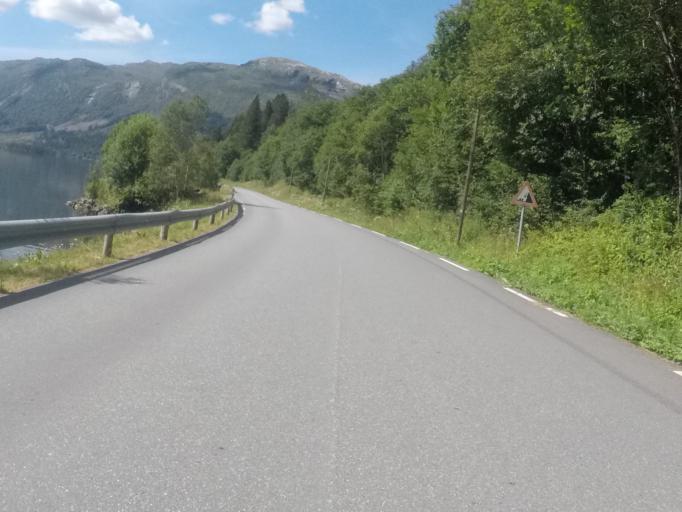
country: NO
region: Sogn og Fjordane
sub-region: Hoyanger
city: Hoyanger
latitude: 61.3586
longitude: 6.1735
